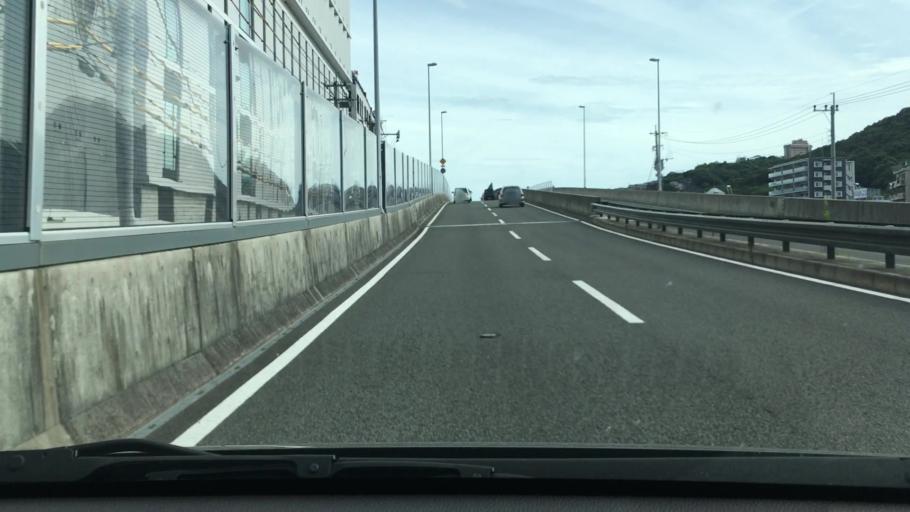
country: JP
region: Nagasaki
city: Nagasaki-shi
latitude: 32.7652
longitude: 129.8622
